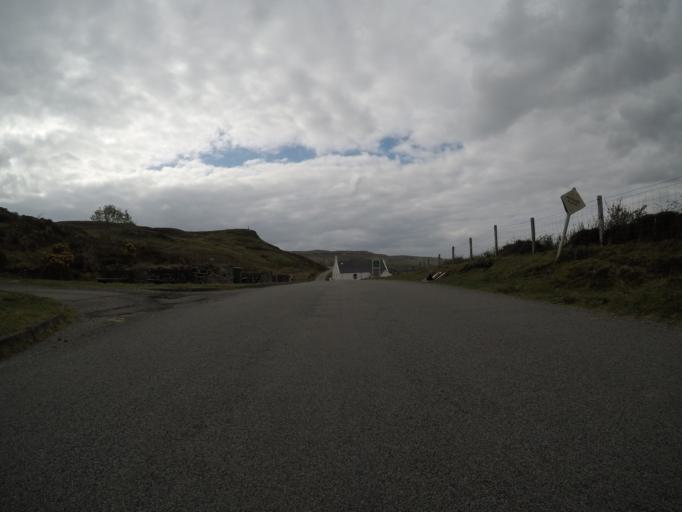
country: GB
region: Scotland
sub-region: Highland
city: Isle of Skye
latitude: 57.2959
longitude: -6.3397
